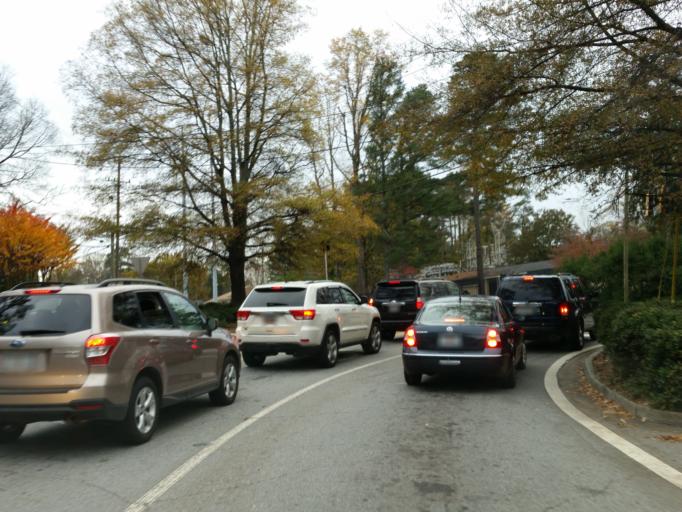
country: US
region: Georgia
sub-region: Fulton County
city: Sandy Springs
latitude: 33.9021
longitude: -84.3784
